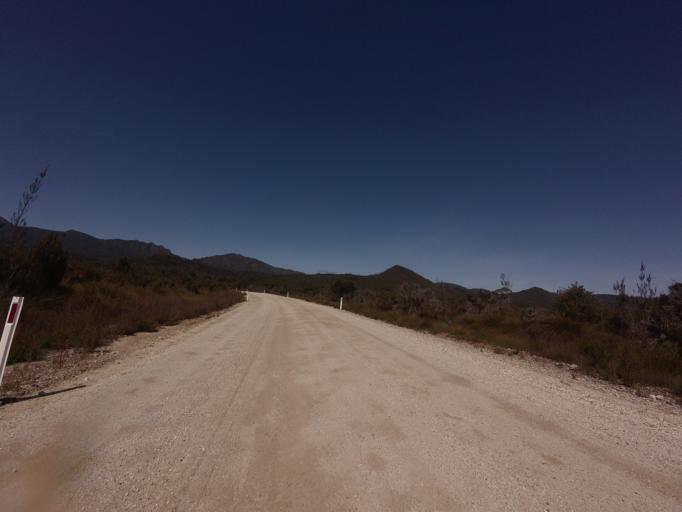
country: AU
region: Tasmania
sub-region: Huon Valley
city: Geeveston
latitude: -42.8938
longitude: 146.3740
